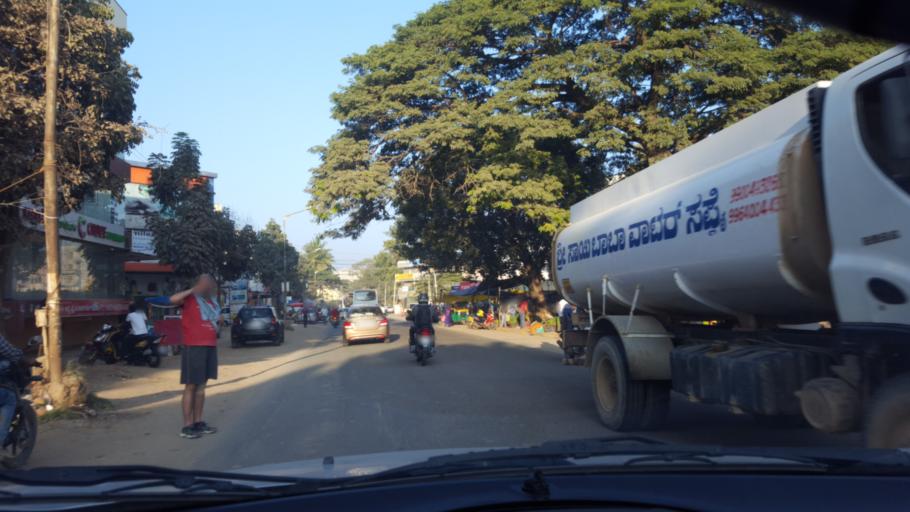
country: IN
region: Karnataka
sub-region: Bangalore Rural
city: Hoskote
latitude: 12.9365
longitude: 77.7447
